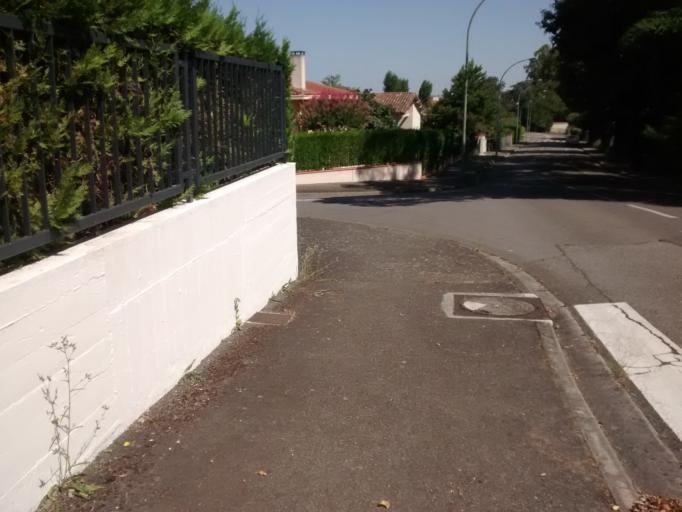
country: FR
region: Midi-Pyrenees
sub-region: Departement de la Haute-Garonne
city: Ramonville-Saint-Agne
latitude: 43.5504
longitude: 1.4665
